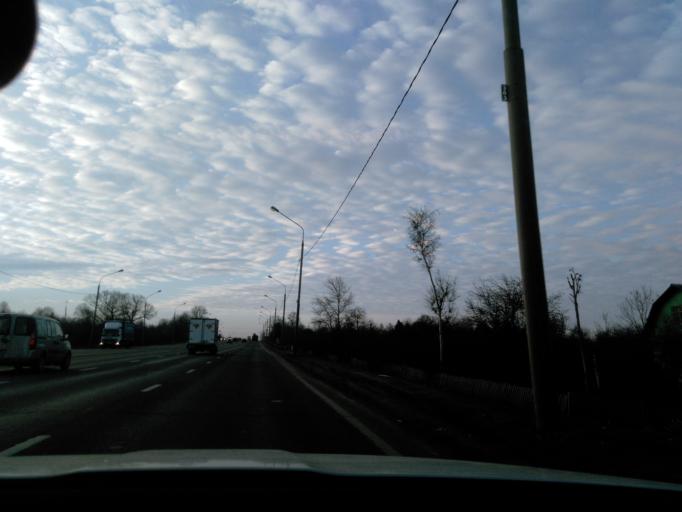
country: RU
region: Moskovskaya
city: Novopodrezkovo
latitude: 55.9291
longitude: 37.3807
